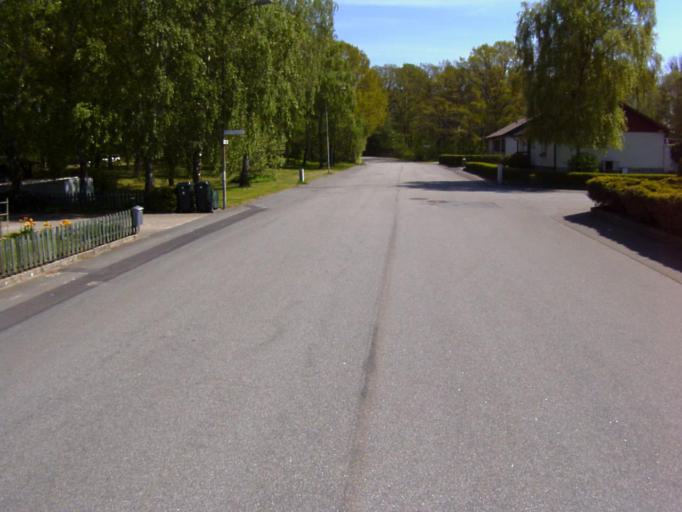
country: SE
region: Skane
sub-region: Kristianstads Kommun
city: Onnestad
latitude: 55.9310
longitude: 13.9884
